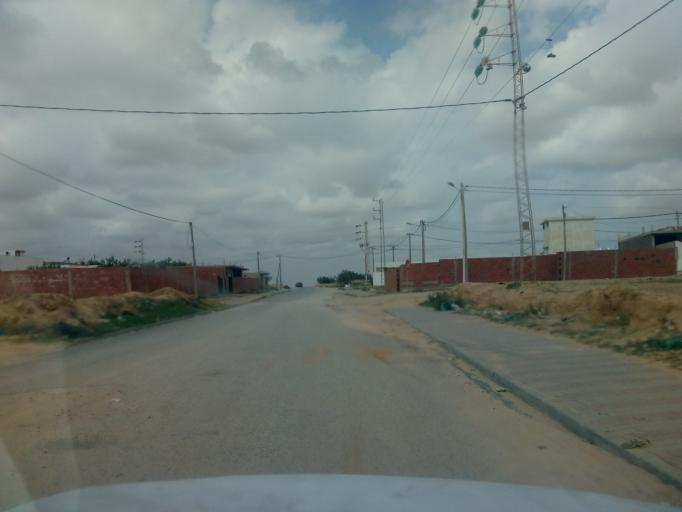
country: TN
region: Safaqis
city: Sfax
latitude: 34.7467
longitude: 10.5138
